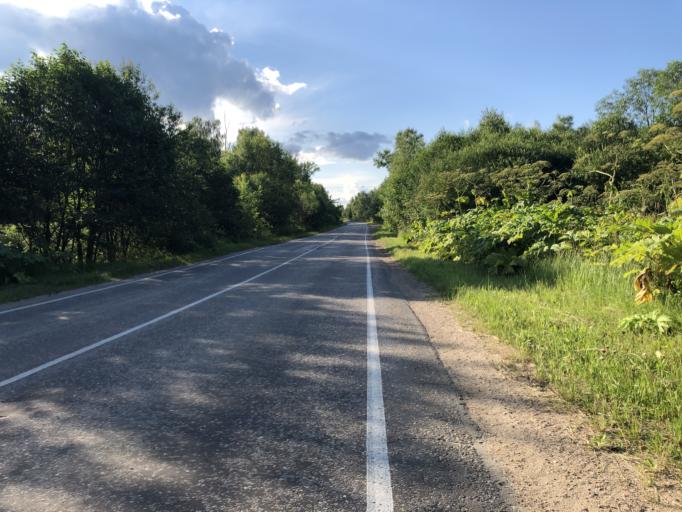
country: RU
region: Tverskaya
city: Rzhev
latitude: 56.2707
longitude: 34.2471
